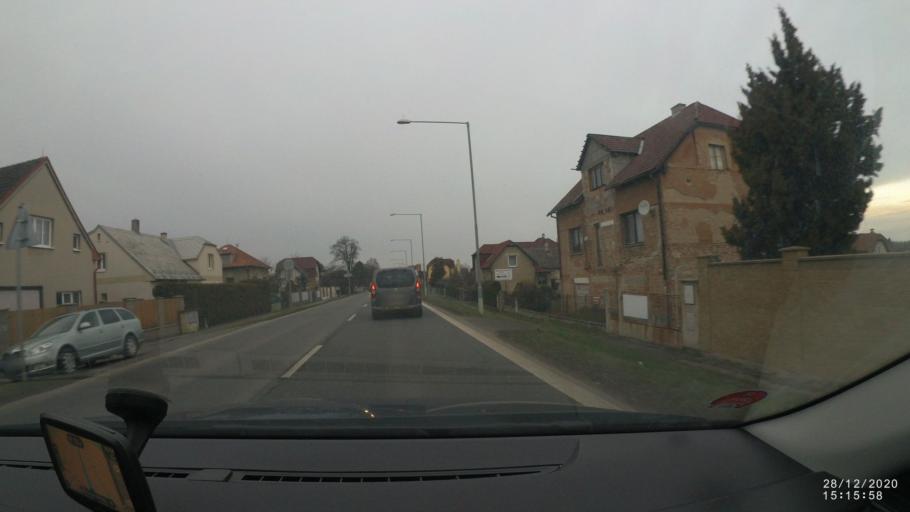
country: CZ
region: Central Bohemia
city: Sestajovice
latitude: 50.0730
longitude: 14.6801
